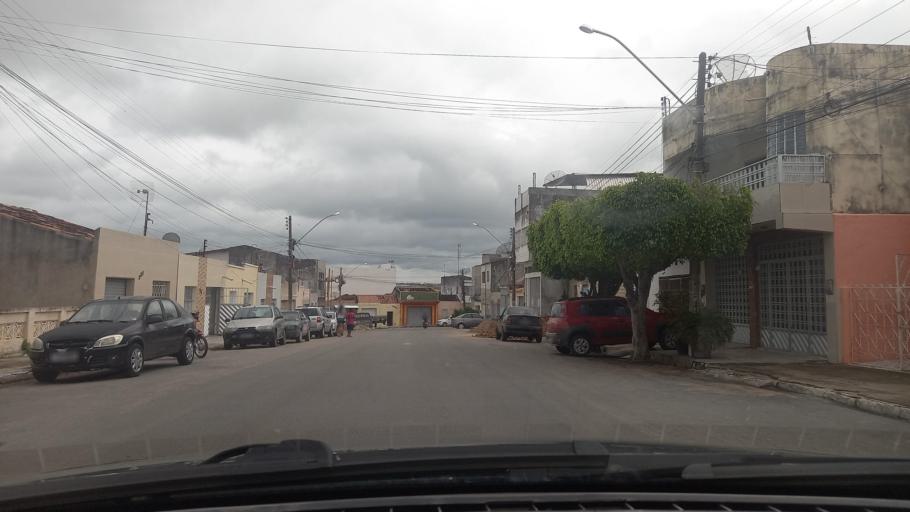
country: BR
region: Alagoas
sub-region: Delmiro Gouveia
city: Delmiro Gouveia
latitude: -9.3850
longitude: -37.9997
